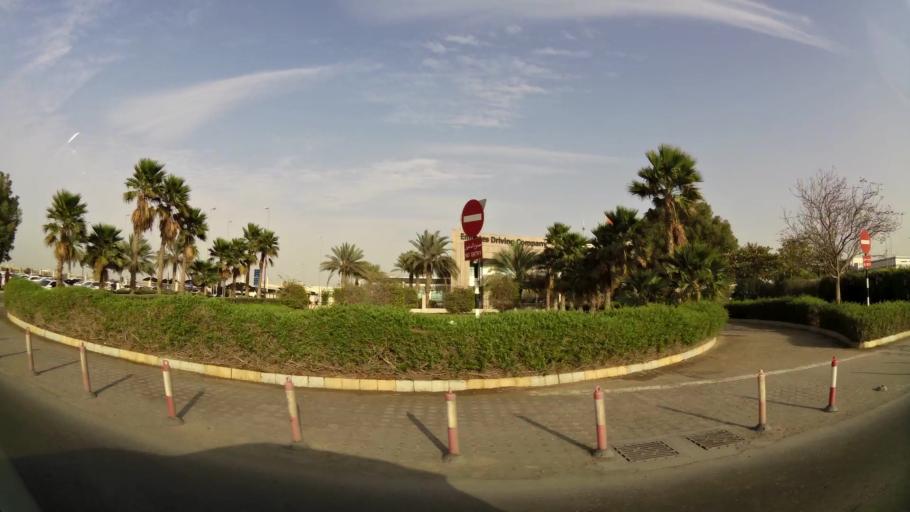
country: AE
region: Abu Dhabi
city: Abu Dhabi
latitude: 24.3443
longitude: 54.5174
